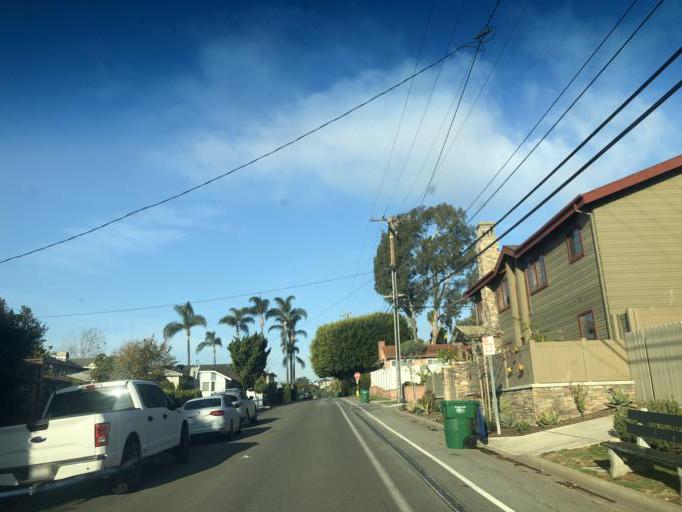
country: US
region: California
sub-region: Orange County
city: Laguna Beach
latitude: 33.5467
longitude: -117.7882
